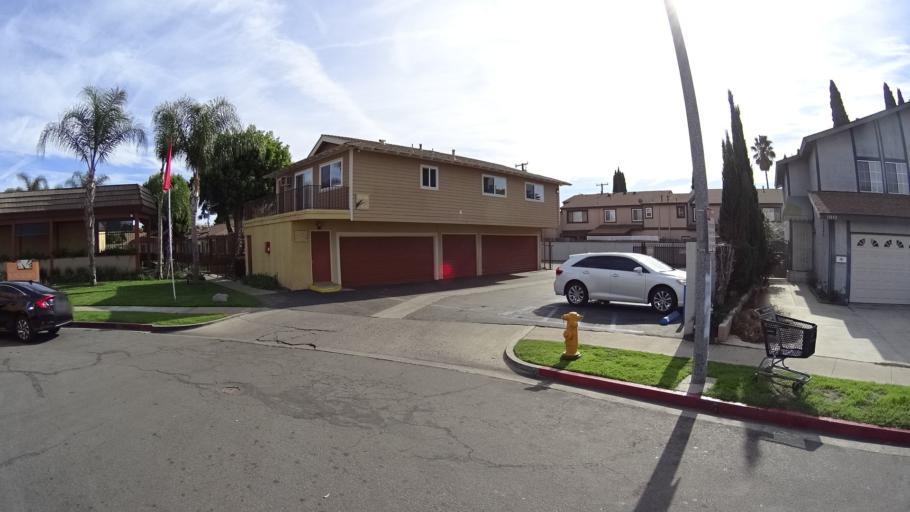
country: US
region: California
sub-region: Orange County
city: Garden Grove
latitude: 33.7621
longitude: -117.9369
